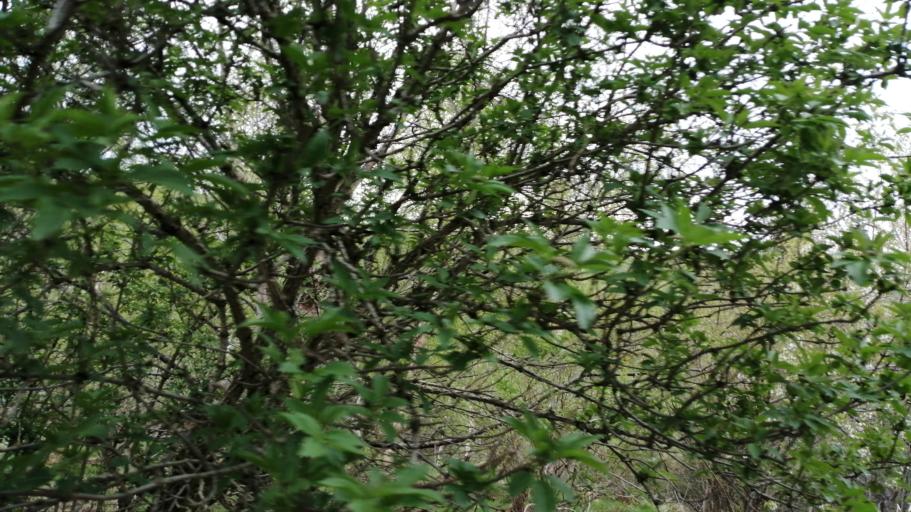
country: GB
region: Scotland
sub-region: Moray
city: Keith
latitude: 57.5359
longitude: -2.9325
